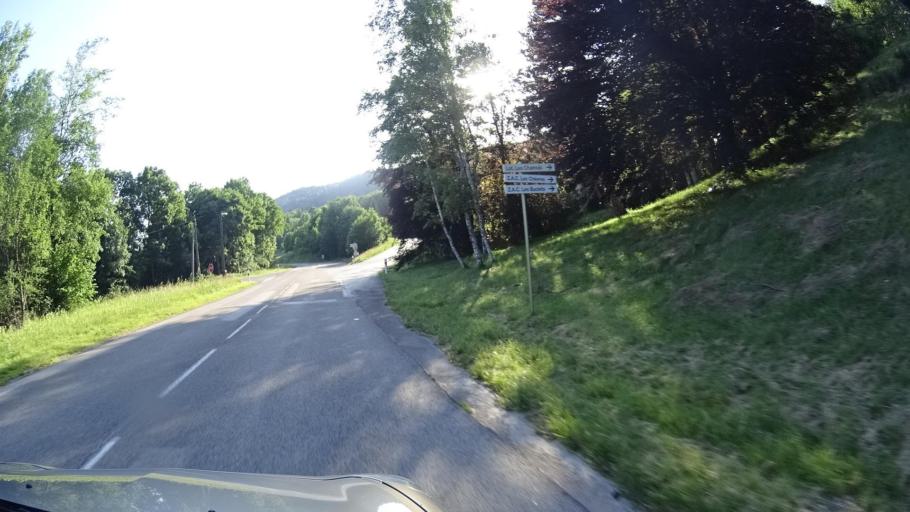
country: FR
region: Franche-Comte
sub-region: Departement du Jura
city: Morbier
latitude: 46.5358
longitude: 6.0036
